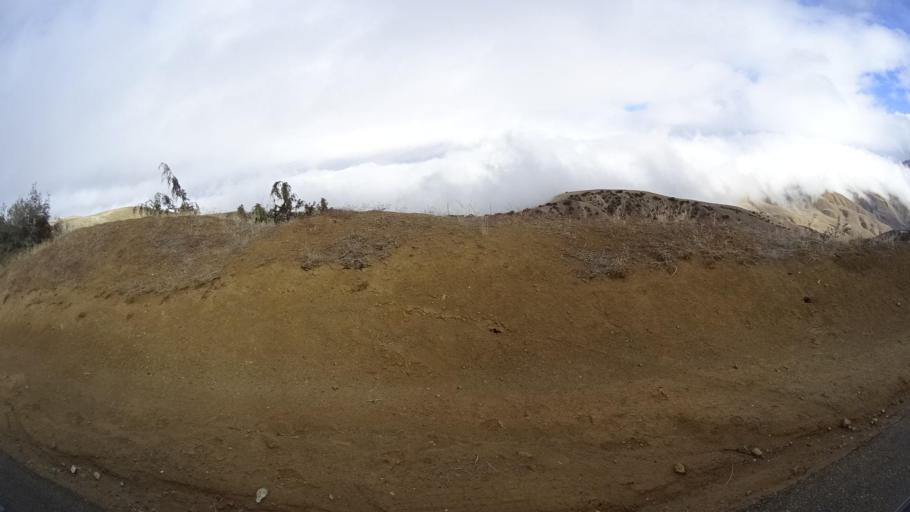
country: US
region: California
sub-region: Kern County
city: Maricopa
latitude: 34.8929
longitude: -119.3600
